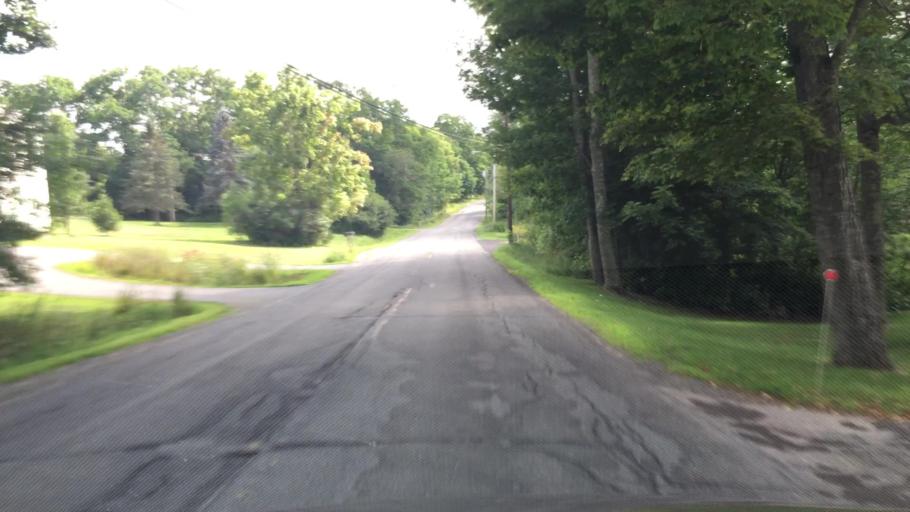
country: US
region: Maine
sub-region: Penobscot County
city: Hampden
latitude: 44.7310
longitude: -68.8614
